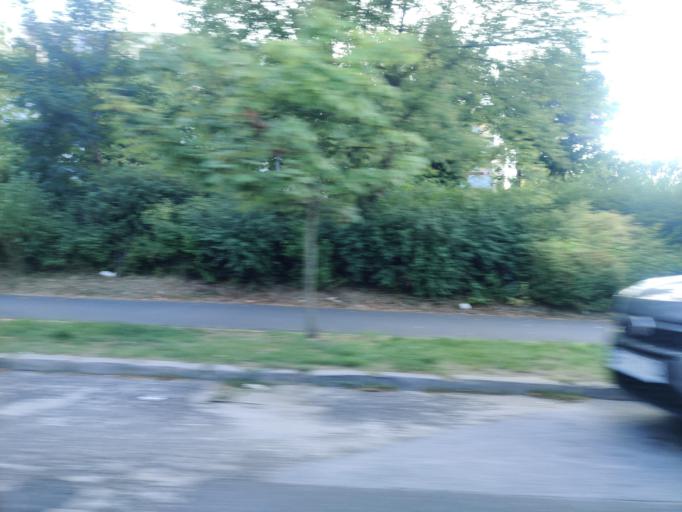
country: PL
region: Greater Poland Voivodeship
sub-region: Konin
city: Konin
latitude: 52.2359
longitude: 18.2612
